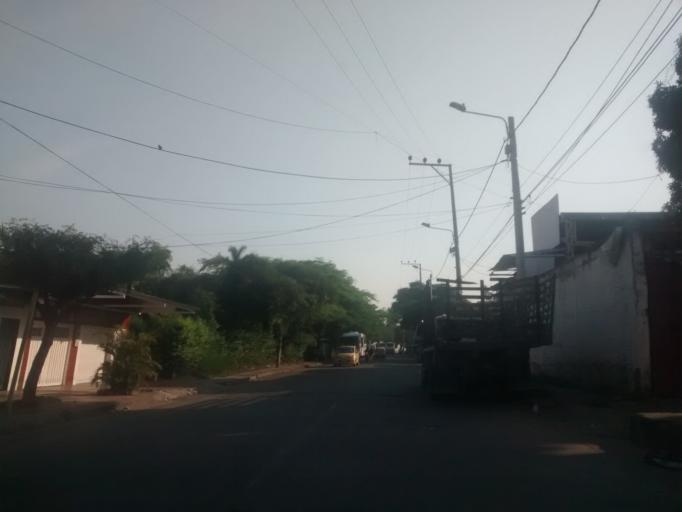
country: CO
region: Cundinamarca
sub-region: Girardot
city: Girardot City
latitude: 4.3030
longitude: -74.7961
